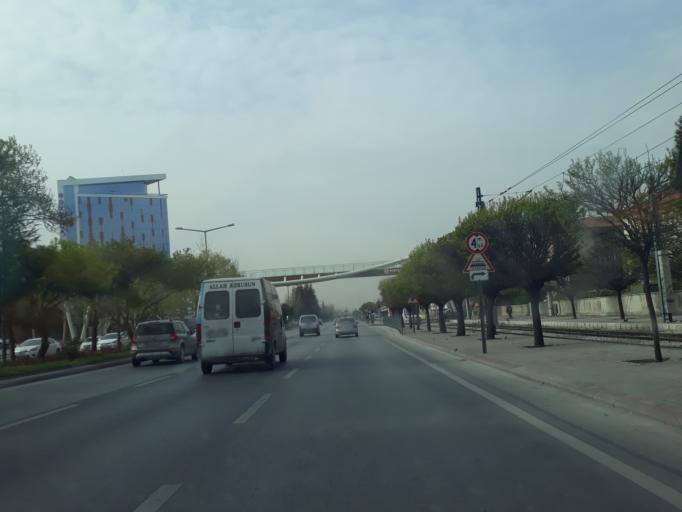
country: TR
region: Konya
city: Selcuklu
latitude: 37.9383
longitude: 32.5112
